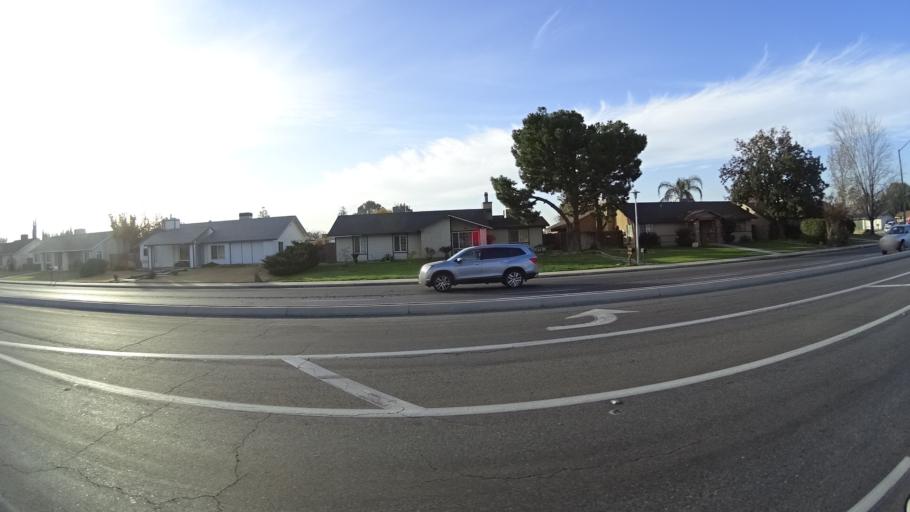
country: US
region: California
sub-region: Kern County
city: Greenacres
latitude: 35.3983
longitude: -119.1179
